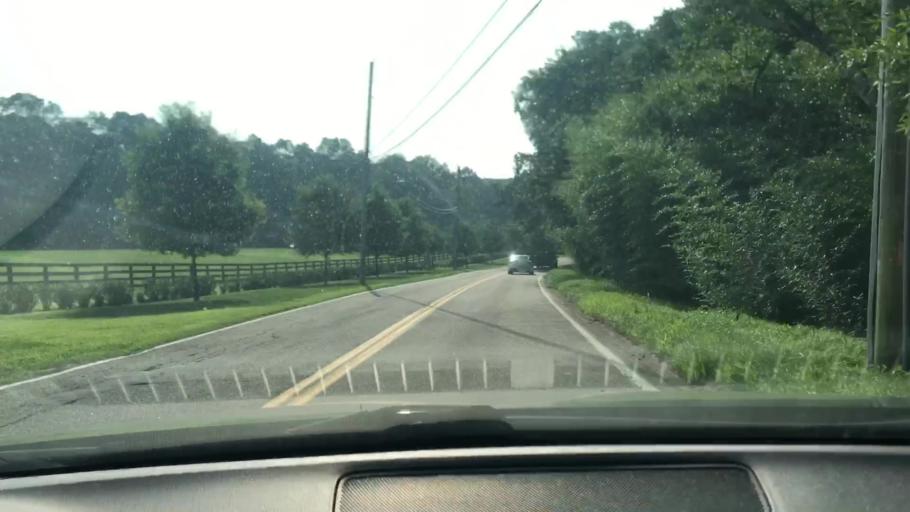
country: US
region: New York
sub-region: Suffolk County
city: Noyack
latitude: 40.9686
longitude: -72.3409
